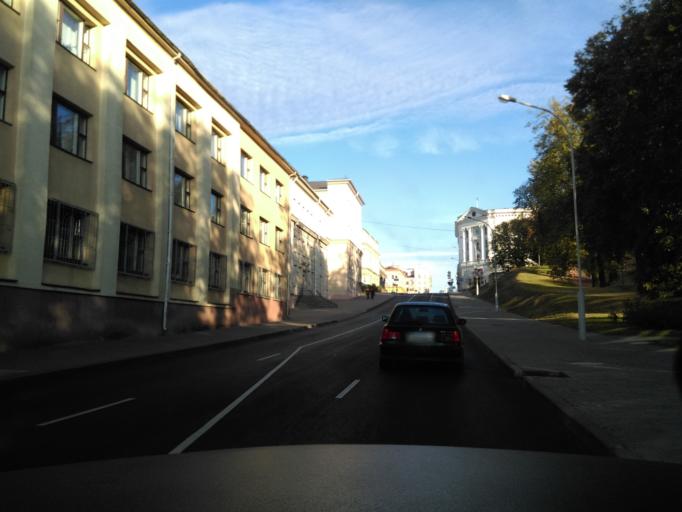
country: BY
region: Minsk
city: Minsk
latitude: 53.8970
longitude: 27.5636
